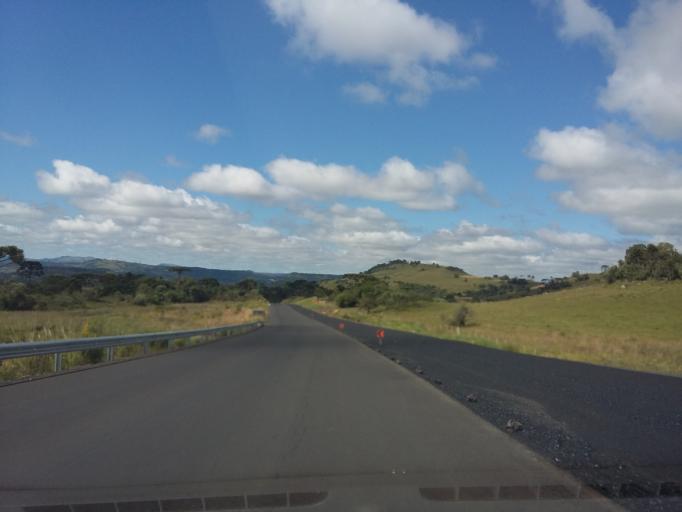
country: BR
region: Santa Catarina
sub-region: Sao Joaquim
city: Sao Joaquim
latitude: -28.0703
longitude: -50.0732
